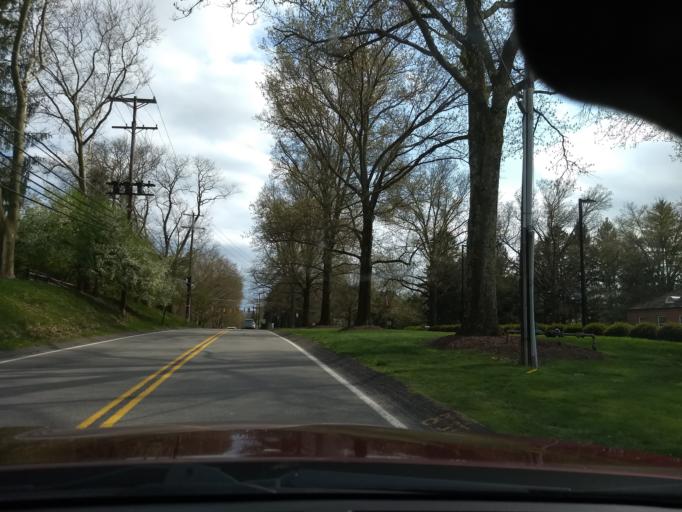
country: US
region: Pennsylvania
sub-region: Allegheny County
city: Fox Chapel
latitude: 40.5151
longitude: -79.8791
